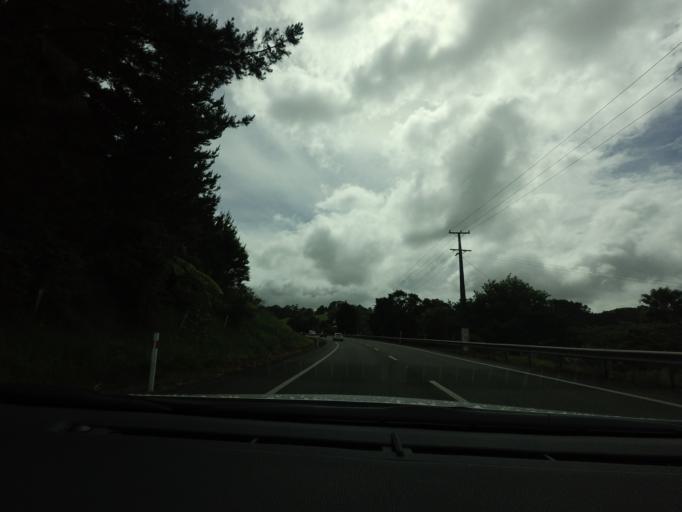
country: NZ
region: Auckland
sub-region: Auckland
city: Warkworth
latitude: -36.5125
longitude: 174.6706
